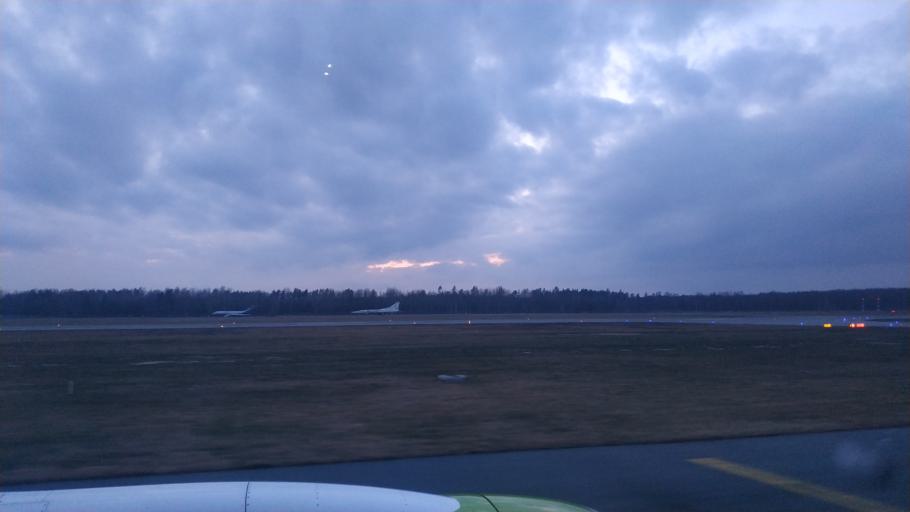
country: LV
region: Babite
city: Pinki
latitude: 56.9280
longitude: 23.9758
